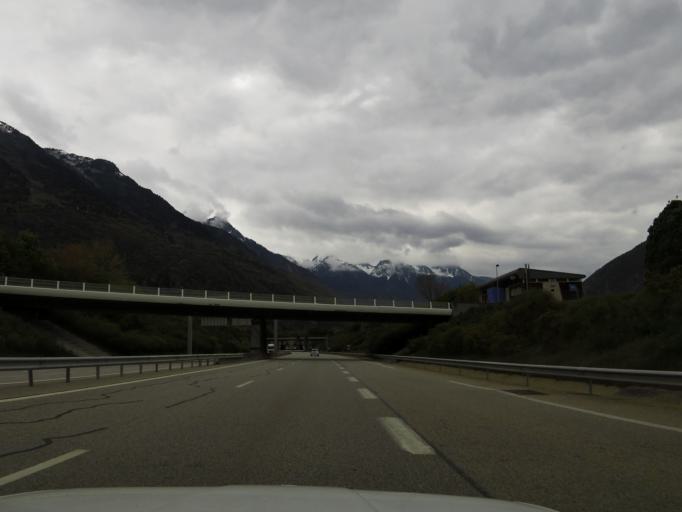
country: FR
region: Rhone-Alpes
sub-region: Departement de la Savoie
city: La Chambre
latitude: 45.3459
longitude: 6.3031
